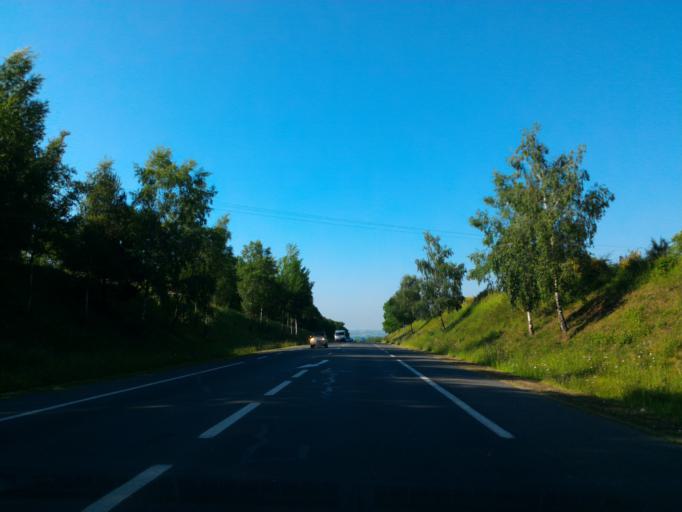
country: FR
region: Brittany
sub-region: Departement d'Ille-et-Vilaine
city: Lecousse
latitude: 48.3615
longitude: -1.2285
